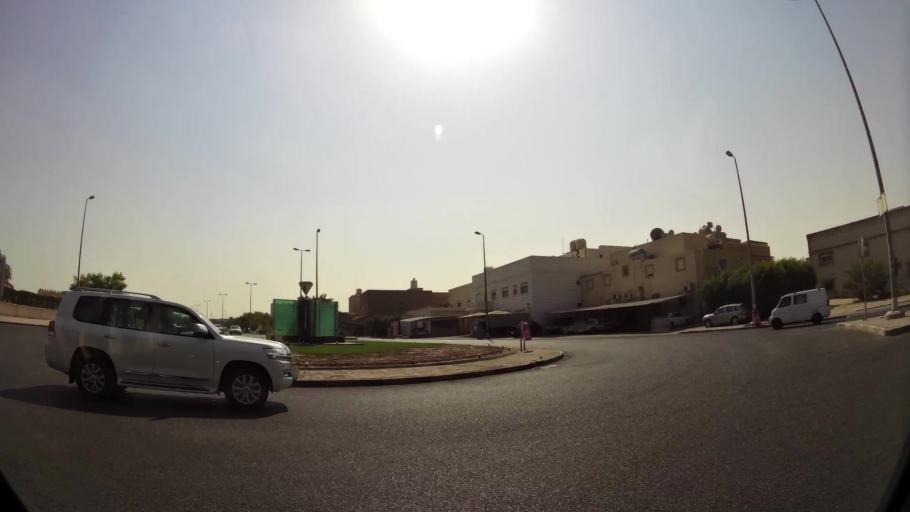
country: KW
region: Al Ahmadi
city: Al Fahahil
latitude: 29.0777
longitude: 48.1244
